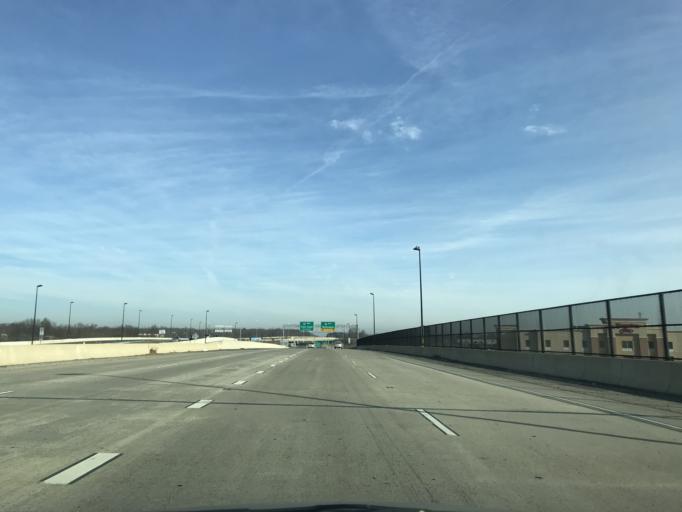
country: US
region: Virginia
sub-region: Prince William County
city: Gainesville
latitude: 38.7968
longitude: -77.6083
